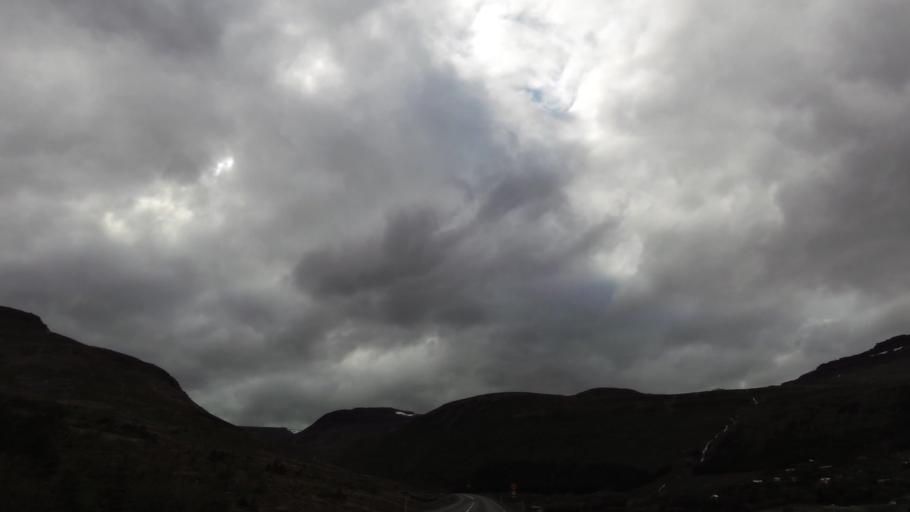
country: IS
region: Westfjords
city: Isafjoerdur
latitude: 66.0573
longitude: -23.1902
